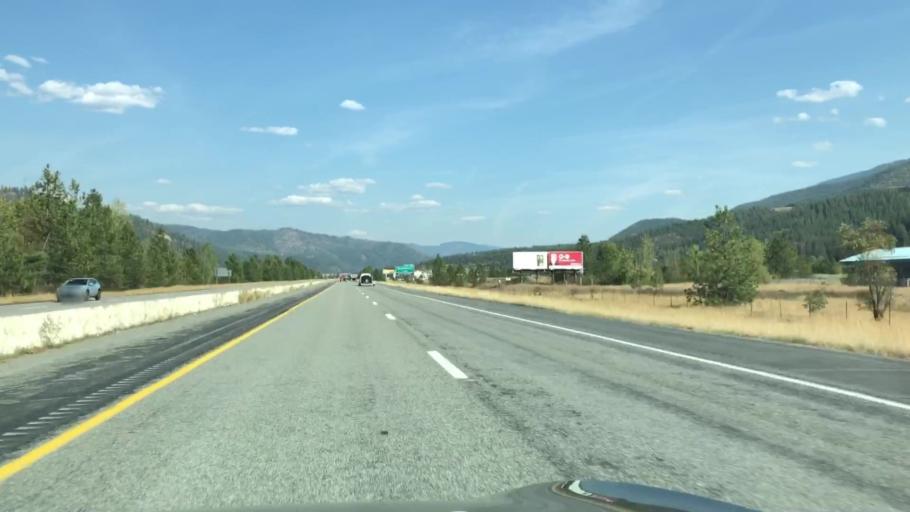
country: US
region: Idaho
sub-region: Shoshone County
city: Pinehurst
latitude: 47.5461
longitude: -116.2047
